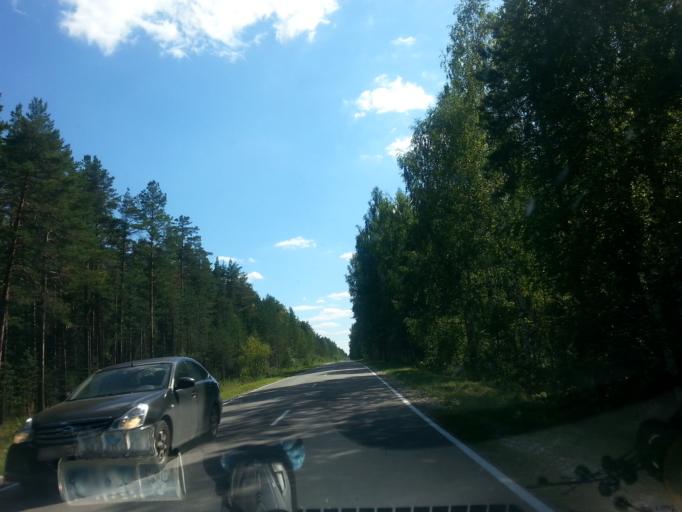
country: RU
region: Vladimir
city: Galitsy
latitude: 56.1183
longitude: 42.8724
